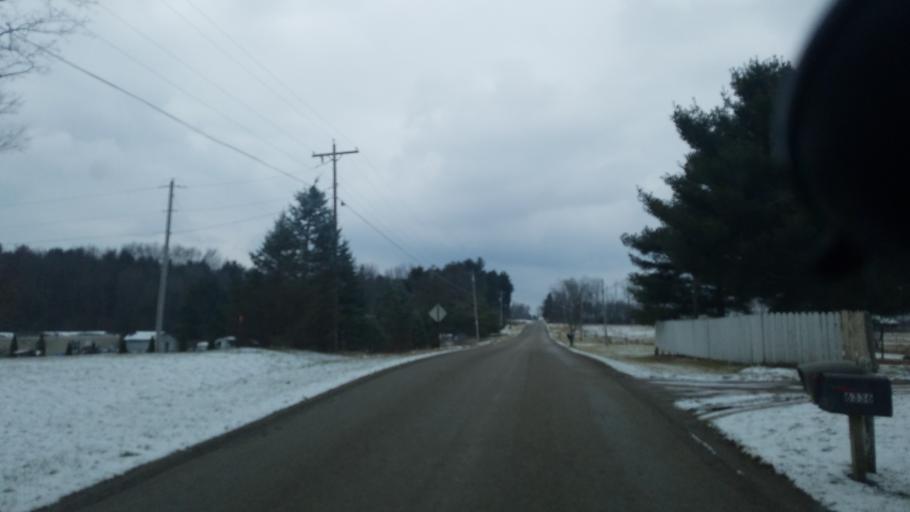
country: US
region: Ohio
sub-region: Morrow County
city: Mount Gilead
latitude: 40.4579
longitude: -82.7085
